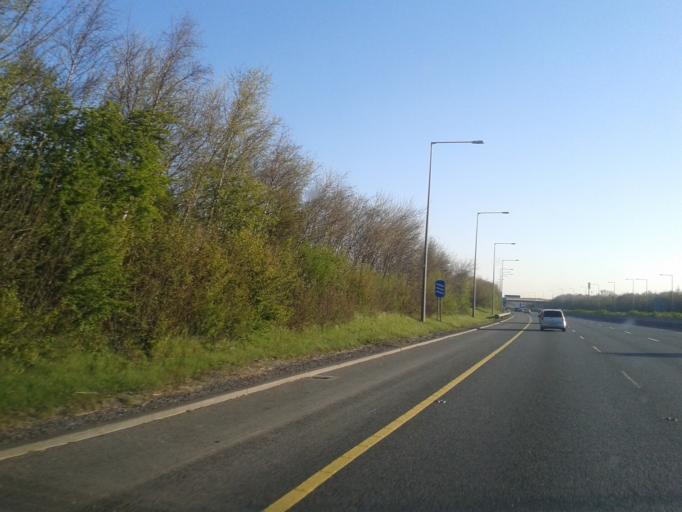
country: IE
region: Leinster
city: Kinsealy-Drinan
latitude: 53.4354
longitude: -6.2115
